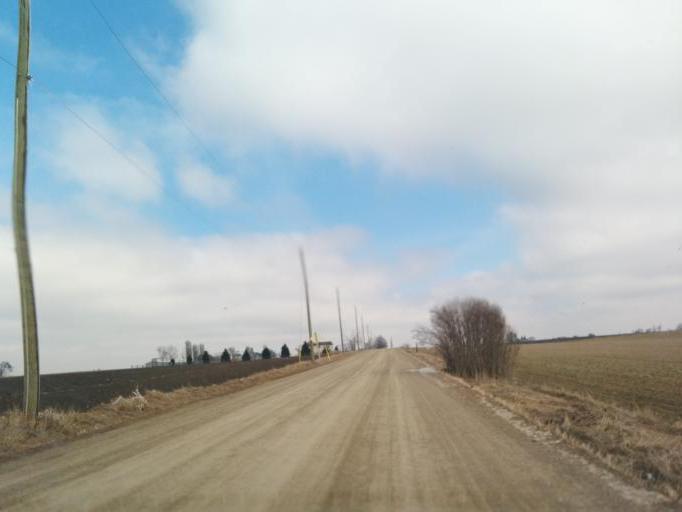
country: CA
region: Ontario
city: Waterloo
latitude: 43.6233
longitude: -80.5482
